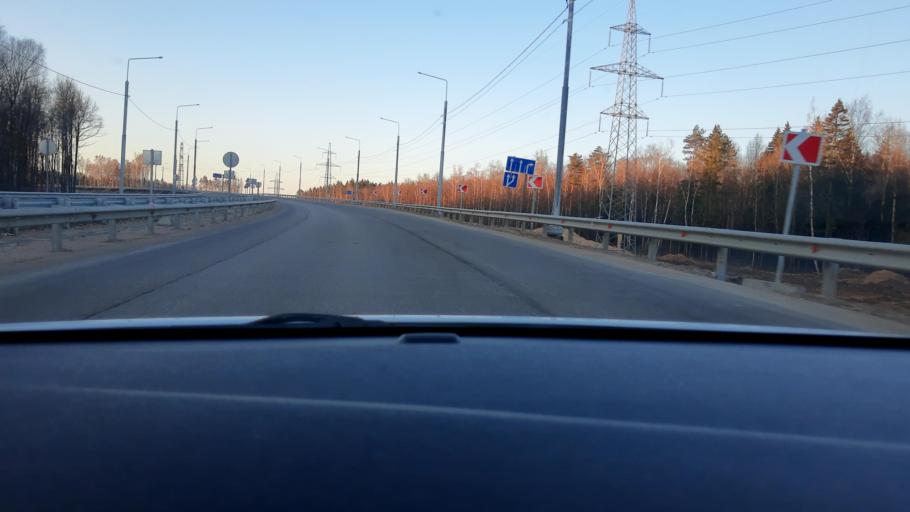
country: RU
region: Moskovskaya
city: Barvikha
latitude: 55.7165
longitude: 37.3119
